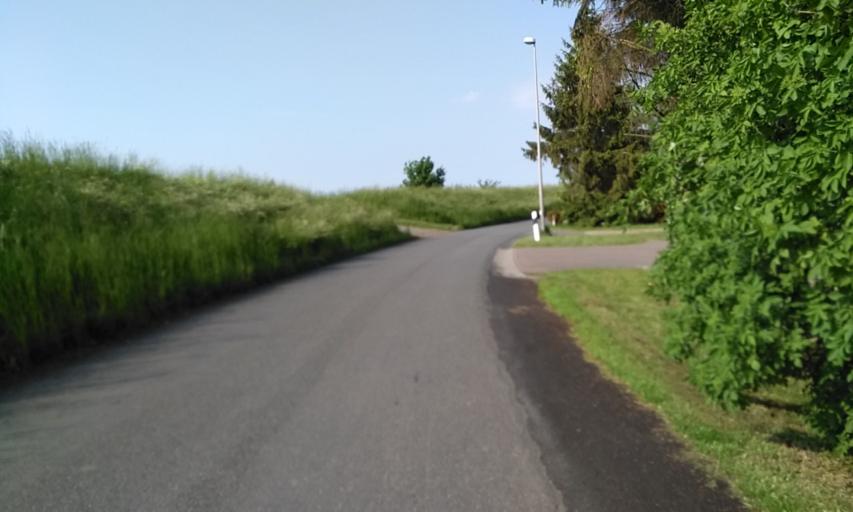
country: DE
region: Lower Saxony
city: Buxtehude
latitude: 53.4945
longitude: 9.7187
